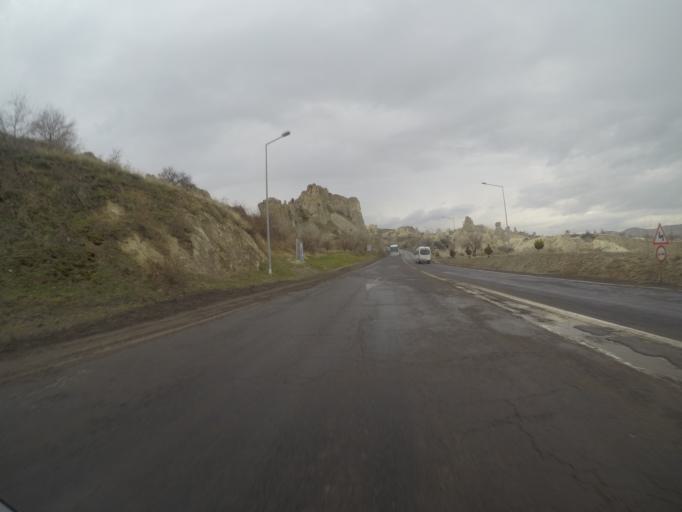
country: TR
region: Nevsehir
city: Urgub
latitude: 38.6337
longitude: 34.8949
